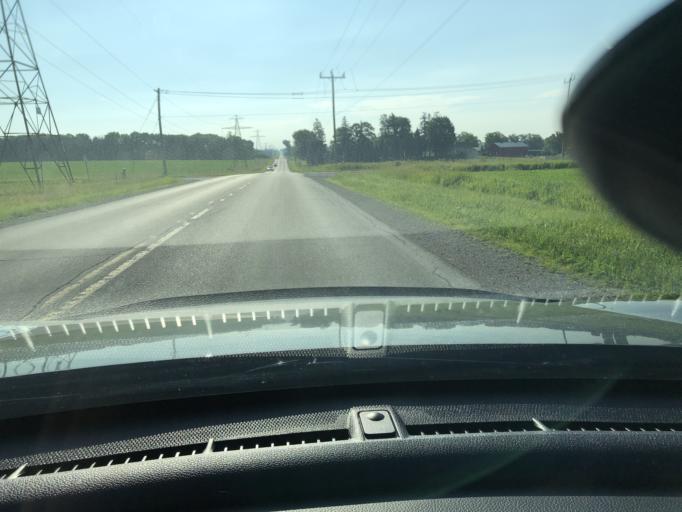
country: CA
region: Ontario
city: Stratford
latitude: 43.3885
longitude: -80.9133
